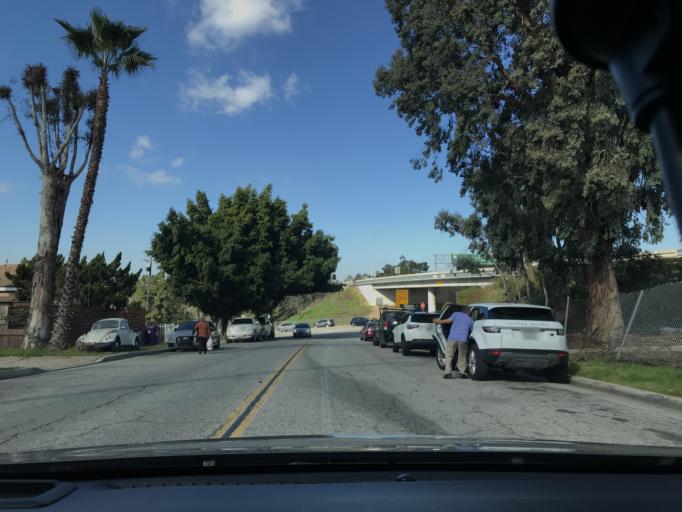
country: US
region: California
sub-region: Los Angeles County
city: Signal Hill
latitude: 33.8181
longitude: -118.1913
